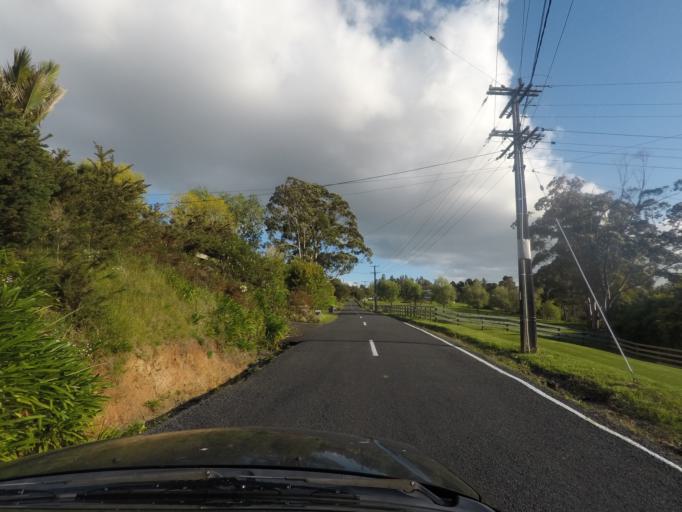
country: NZ
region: Auckland
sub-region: Auckland
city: Titirangi
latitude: -36.9382
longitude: 174.6199
